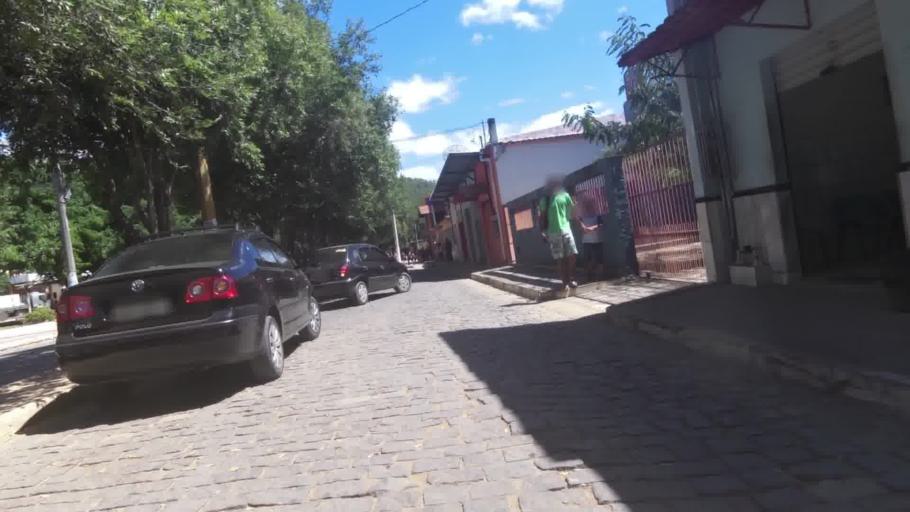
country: BR
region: Espirito Santo
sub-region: Cachoeiro De Itapemirim
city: Cachoeiro de Itapemirim
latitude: -20.9153
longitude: -41.1939
